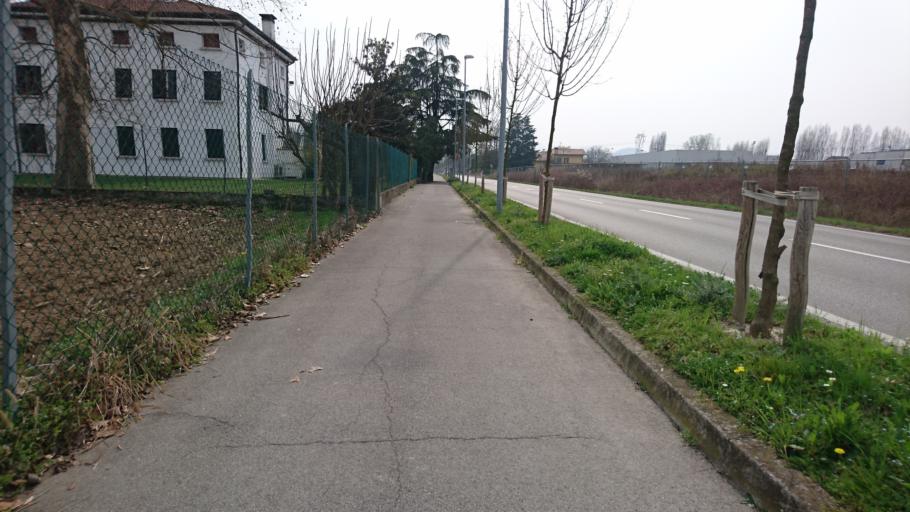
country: IT
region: Veneto
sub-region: Provincia di Padova
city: Saccolongo
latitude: 45.3913
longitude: 11.7679
